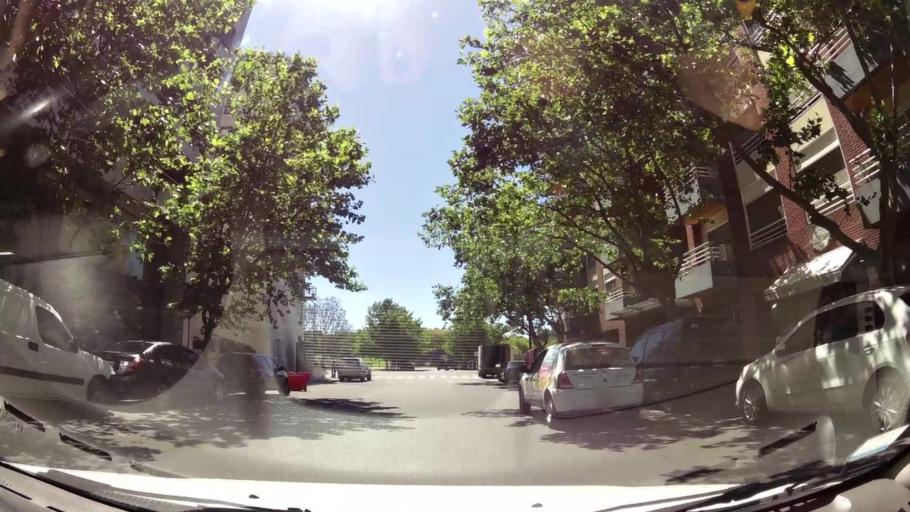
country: AR
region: Buenos Aires F.D.
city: Buenos Aires
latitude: -34.6161
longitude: -58.3618
